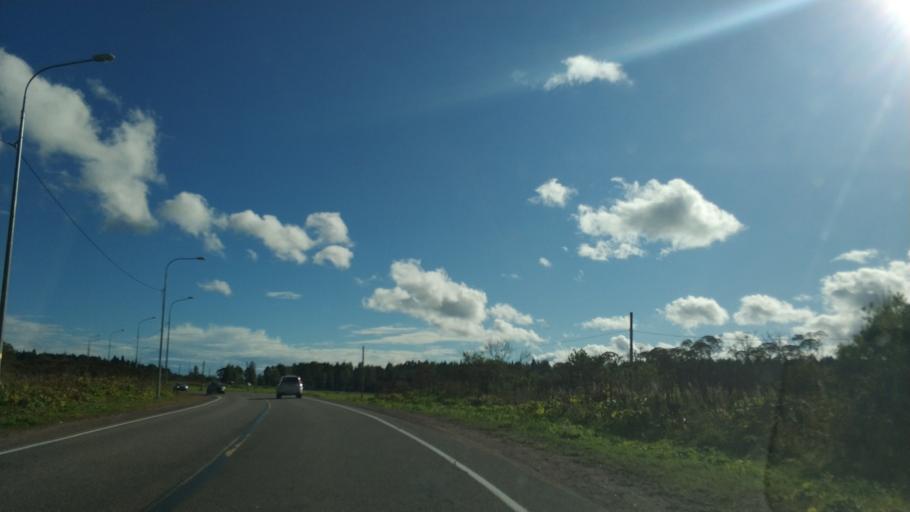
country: RU
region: Republic of Karelia
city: Khelyulya
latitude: 61.6455
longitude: 30.5827
